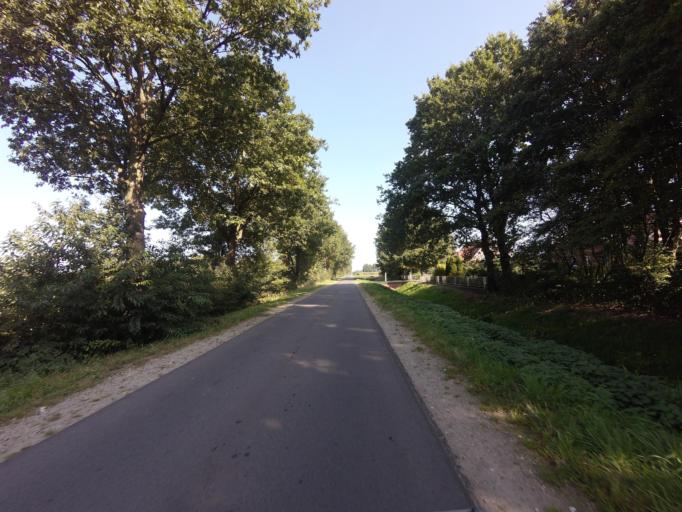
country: DE
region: Lower Saxony
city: Laar
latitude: 52.5776
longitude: 6.7801
